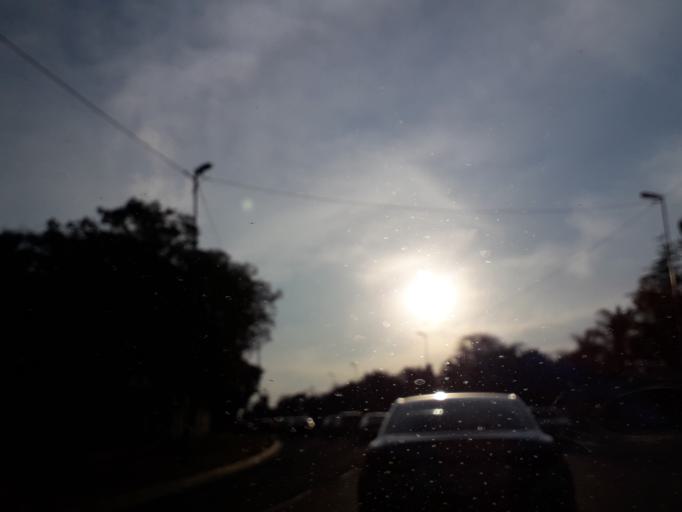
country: ZA
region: Gauteng
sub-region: City of Johannesburg Metropolitan Municipality
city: Diepsloot
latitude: -26.0073
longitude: 28.0054
